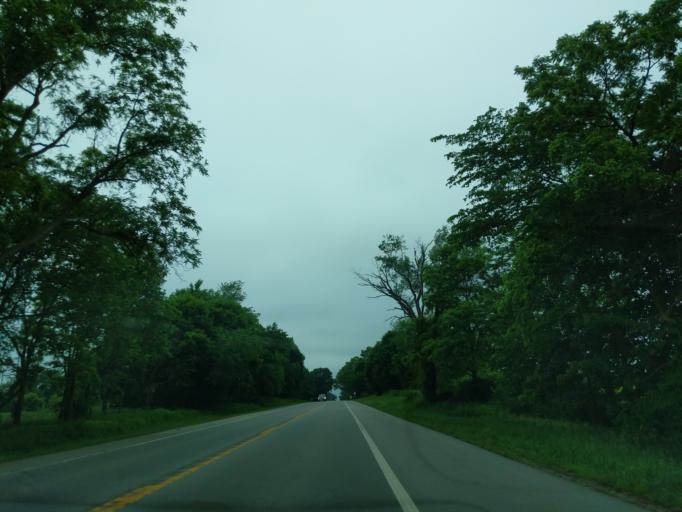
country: US
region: Michigan
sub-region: Branch County
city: Quincy
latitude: 41.9488
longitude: -84.8351
